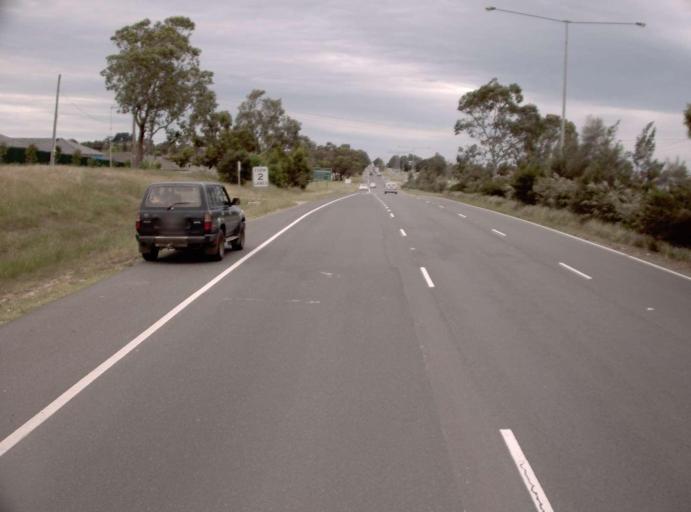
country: AU
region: Victoria
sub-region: Casey
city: Hampton Park
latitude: -38.0432
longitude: 145.2528
